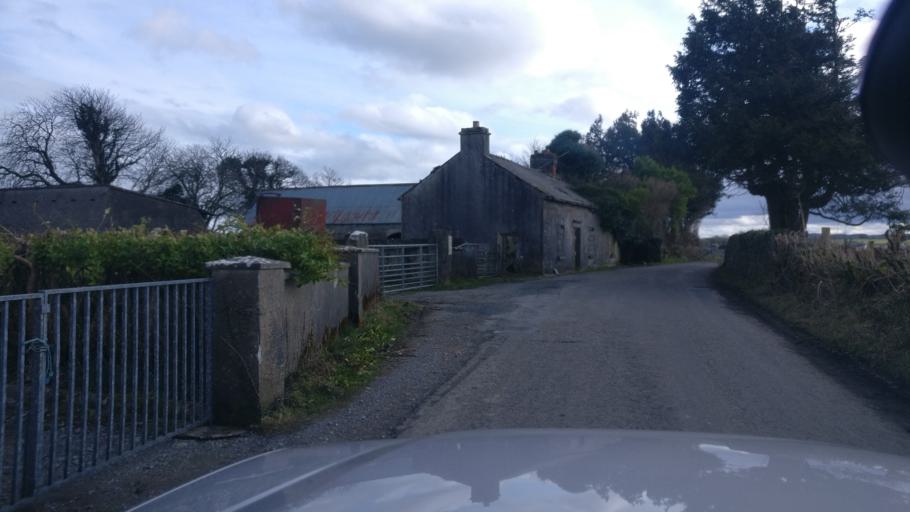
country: IE
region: Connaught
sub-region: County Galway
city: Loughrea
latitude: 53.2013
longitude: -8.5433
